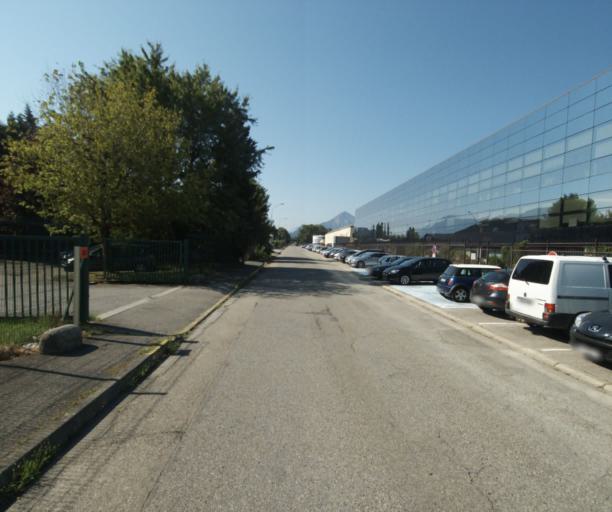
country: FR
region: Rhone-Alpes
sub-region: Departement de l'Isere
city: Le Pont-de-Claix
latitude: 45.1383
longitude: 5.6943
